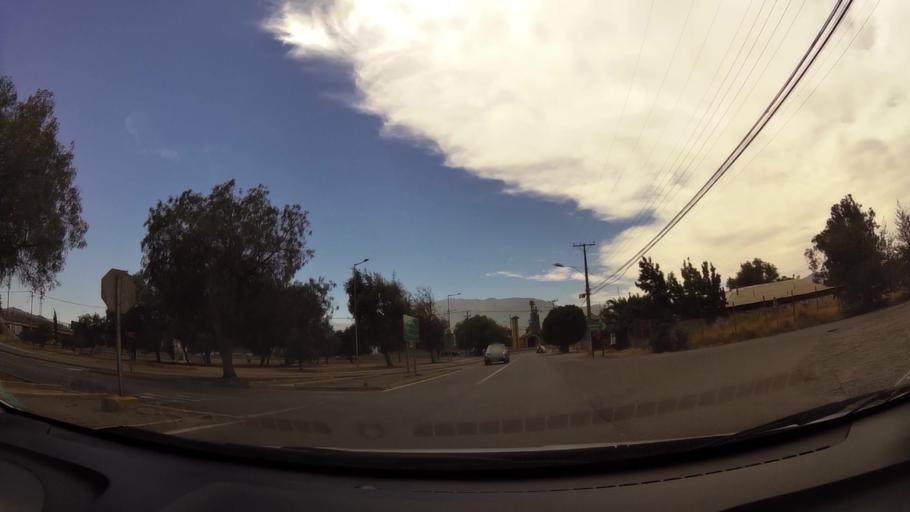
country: CL
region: O'Higgins
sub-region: Provincia de Cachapoal
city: Graneros
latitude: -33.9781
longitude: -70.7056
